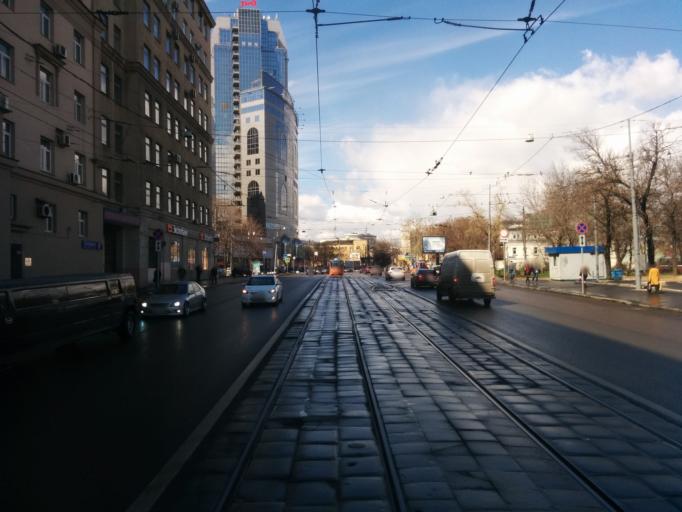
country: RU
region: Moscow
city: Sokol'niki
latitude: 55.7754
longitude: 37.6508
